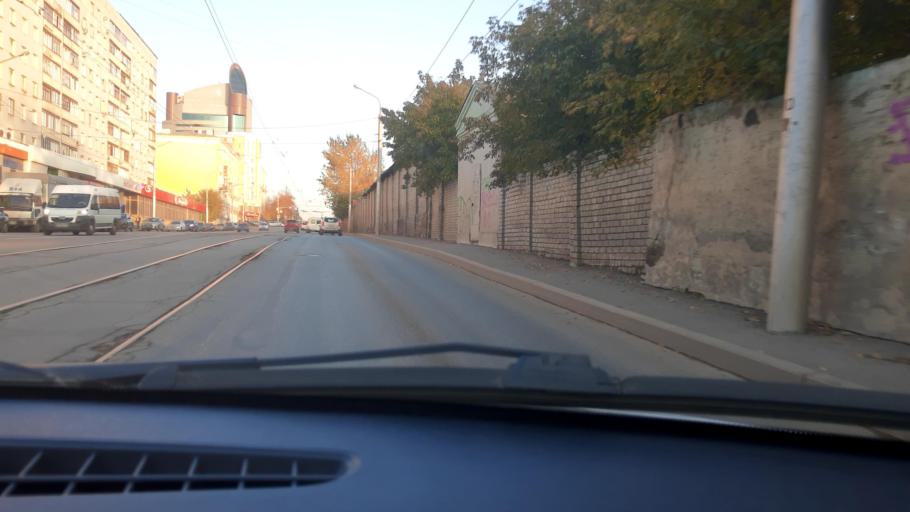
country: RU
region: Bashkortostan
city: Ufa
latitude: 54.7373
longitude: 55.9426
